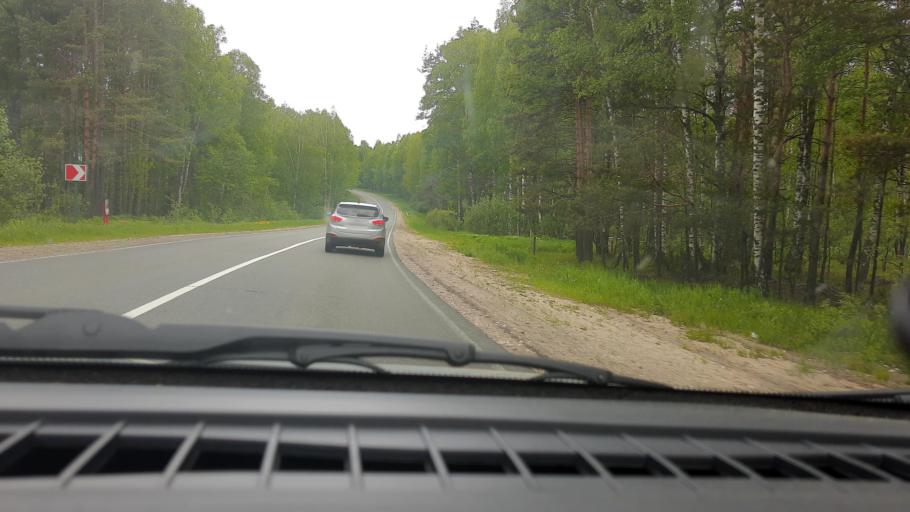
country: RU
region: Nizjnij Novgorod
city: Sukhobezvodnoye
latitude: 56.8555
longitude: 44.8041
